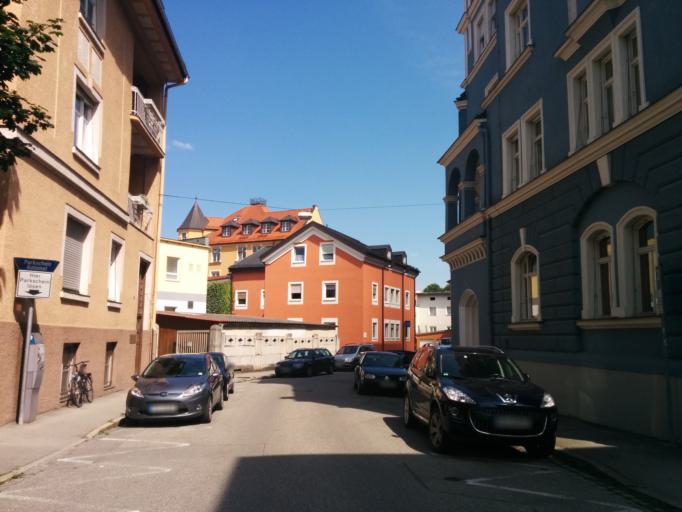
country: DE
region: Bavaria
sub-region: Upper Bavaria
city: Rosenheim
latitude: 47.8544
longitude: 12.1298
